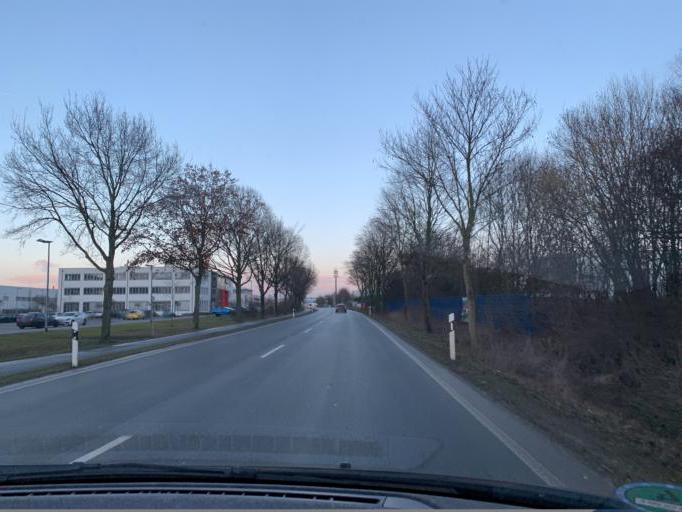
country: DE
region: North Rhine-Westphalia
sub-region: Regierungsbezirk Dusseldorf
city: Juchen
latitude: 51.1000
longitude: 6.5217
